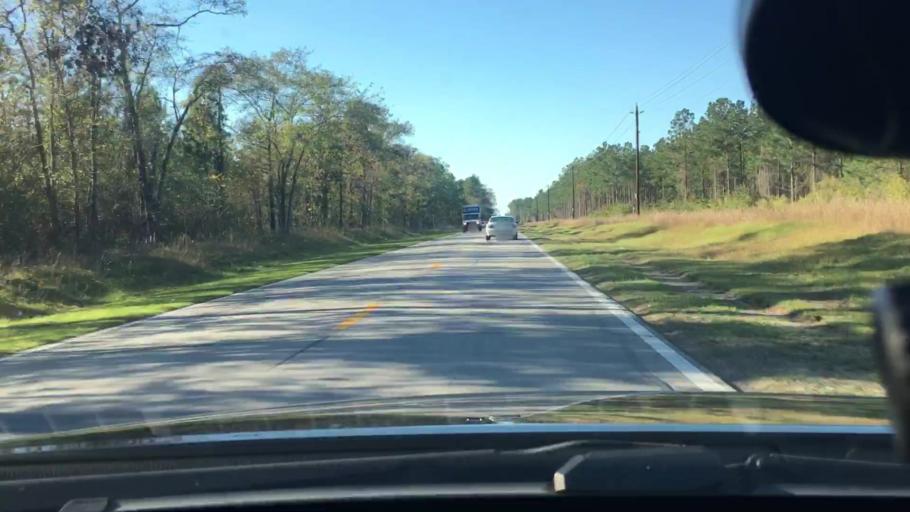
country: US
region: North Carolina
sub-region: Craven County
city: Vanceboro
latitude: 35.2223
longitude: -77.1271
